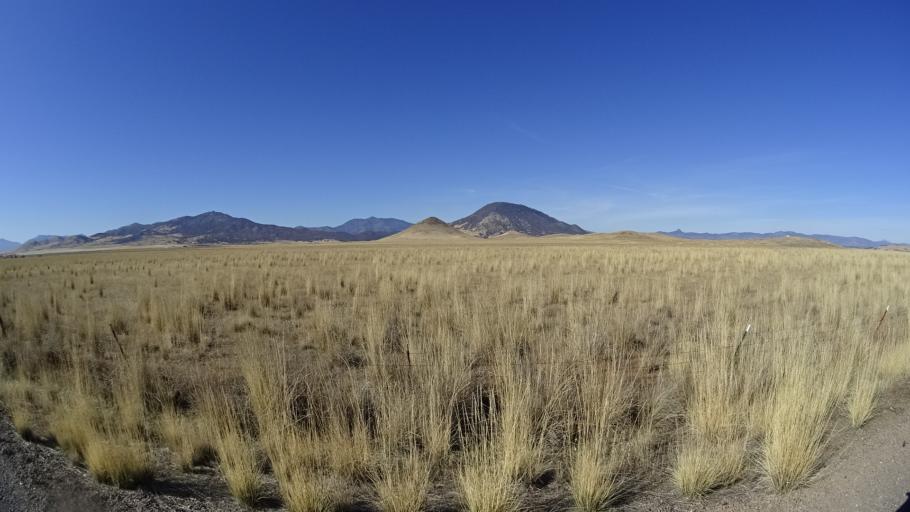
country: US
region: California
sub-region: Siskiyou County
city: Montague
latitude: 41.8042
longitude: -122.4444
